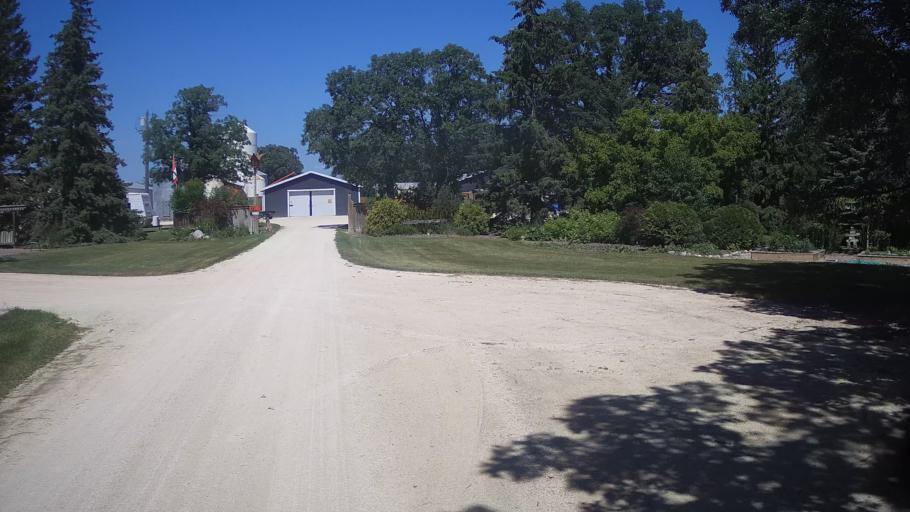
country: CA
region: Manitoba
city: Stonewall
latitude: 50.1242
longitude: -97.4756
